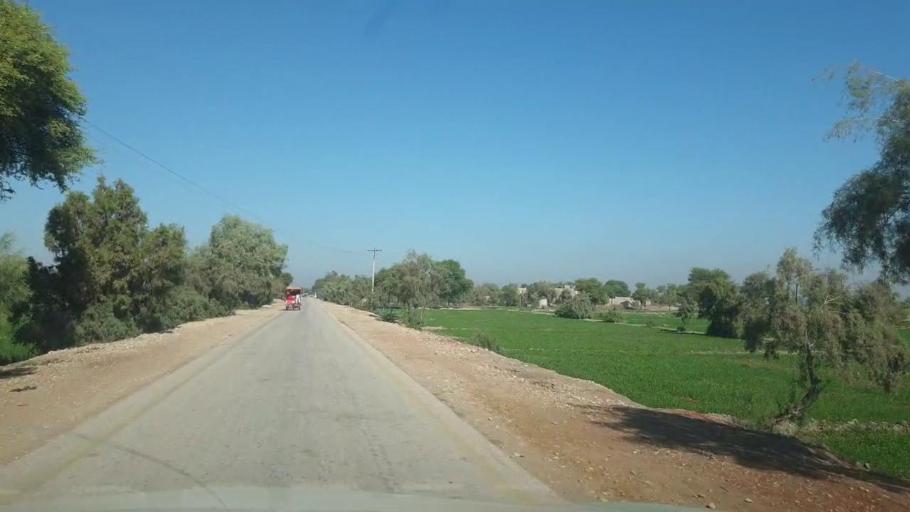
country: PK
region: Sindh
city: Bhan
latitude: 26.5425
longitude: 67.6351
